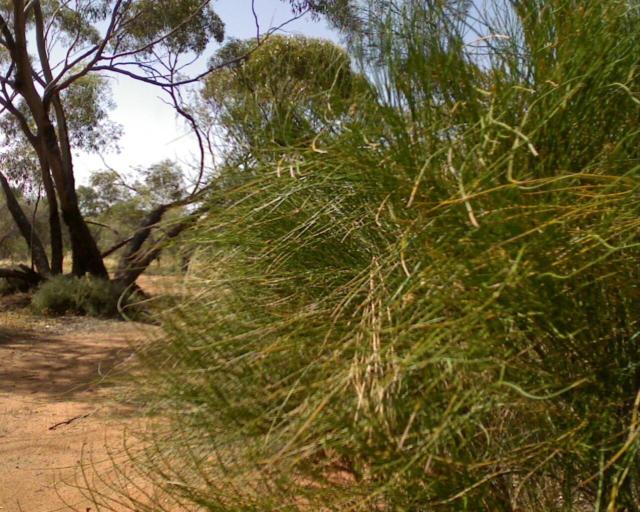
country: AU
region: Western Australia
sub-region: Merredin
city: Merredin
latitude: -30.9547
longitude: 118.8809
